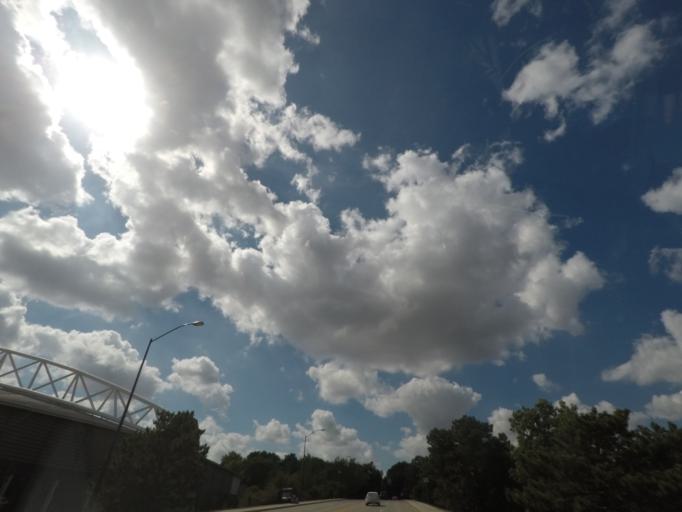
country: US
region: Iowa
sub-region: Story County
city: Ames
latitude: 42.0163
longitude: -93.6374
